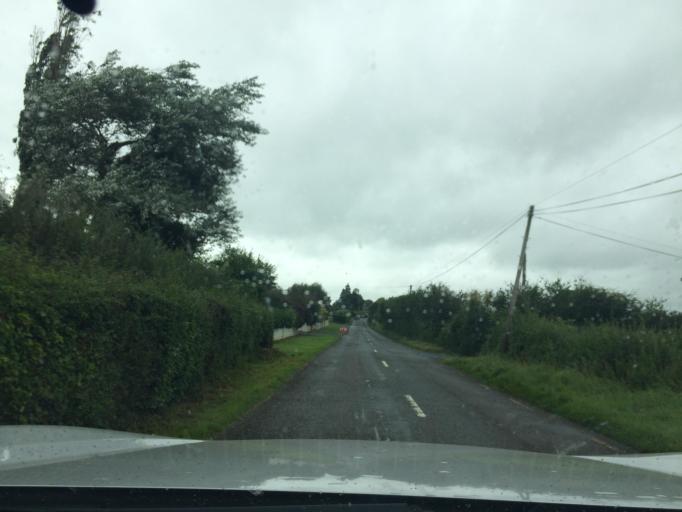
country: IE
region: Munster
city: Thurles
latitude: 52.6199
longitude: -7.8795
